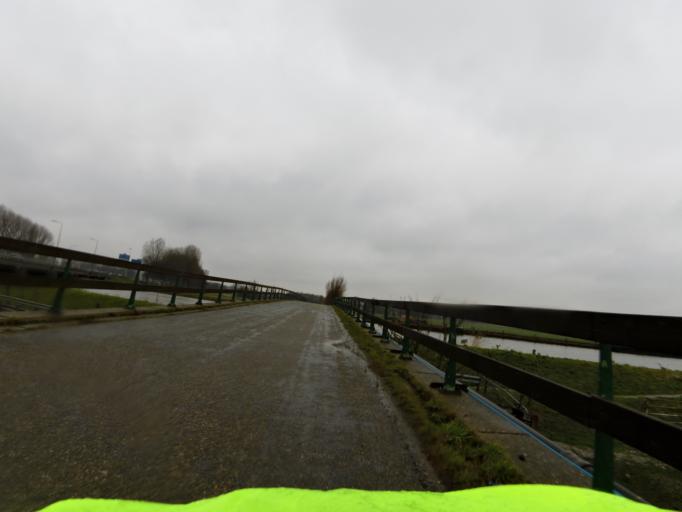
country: NL
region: South Holland
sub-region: Gemeente Maassluis
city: Maassluis
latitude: 51.9235
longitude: 4.2815
